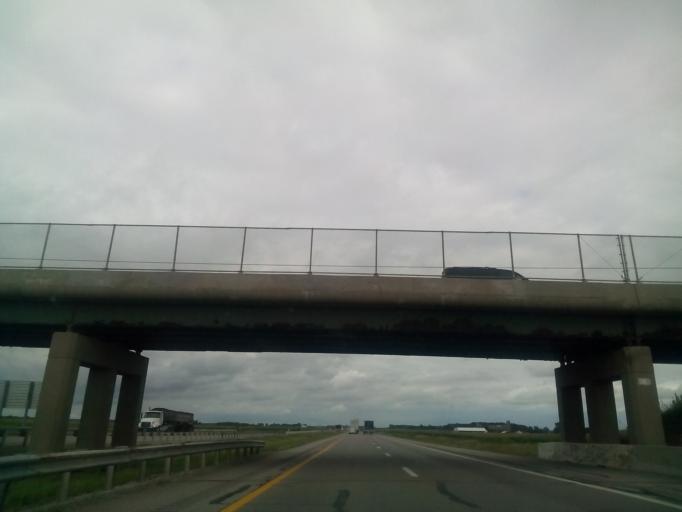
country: US
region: Ohio
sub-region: Fulton County
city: Burlington
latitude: 41.5904
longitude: -84.2882
